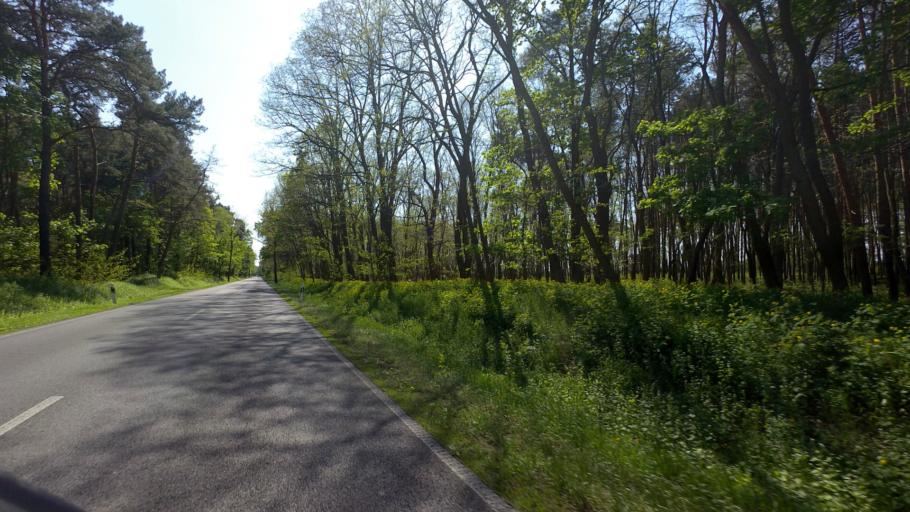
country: DE
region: Brandenburg
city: Tauche
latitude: 52.1264
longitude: 14.1964
